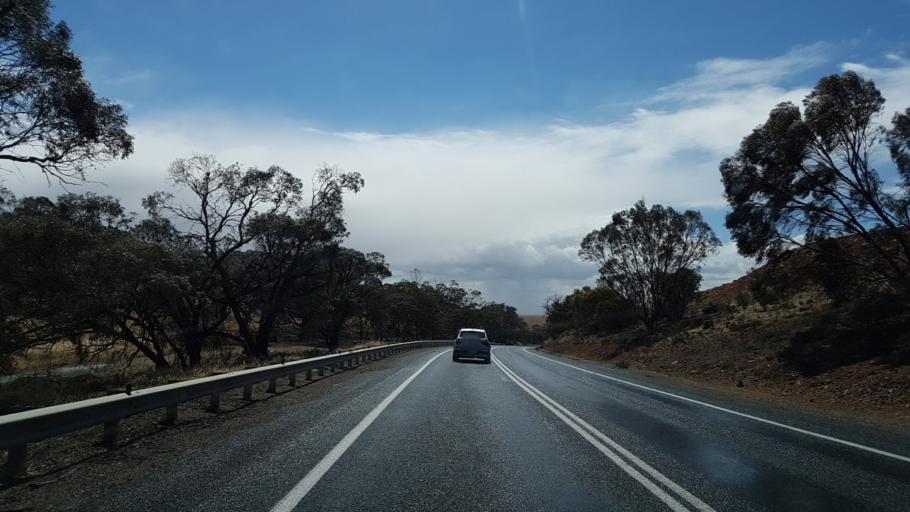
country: AU
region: South Australia
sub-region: Barossa
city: Angaston
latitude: -34.4007
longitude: 139.1938
